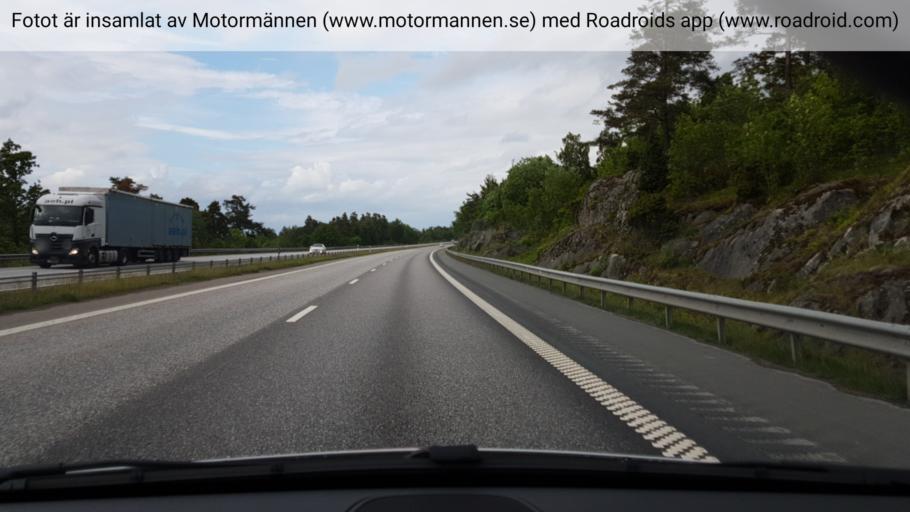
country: SE
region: Joenkoeping
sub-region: Jonkopings Kommun
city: Kaxholmen
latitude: 57.9581
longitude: 14.3513
